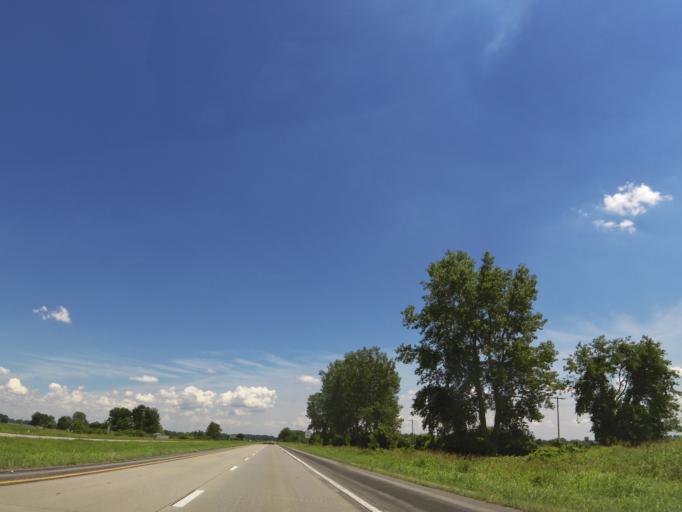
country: US
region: Missouri
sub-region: Pemiscot County
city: Caruthersville
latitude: 36.1479
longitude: -89.6555
